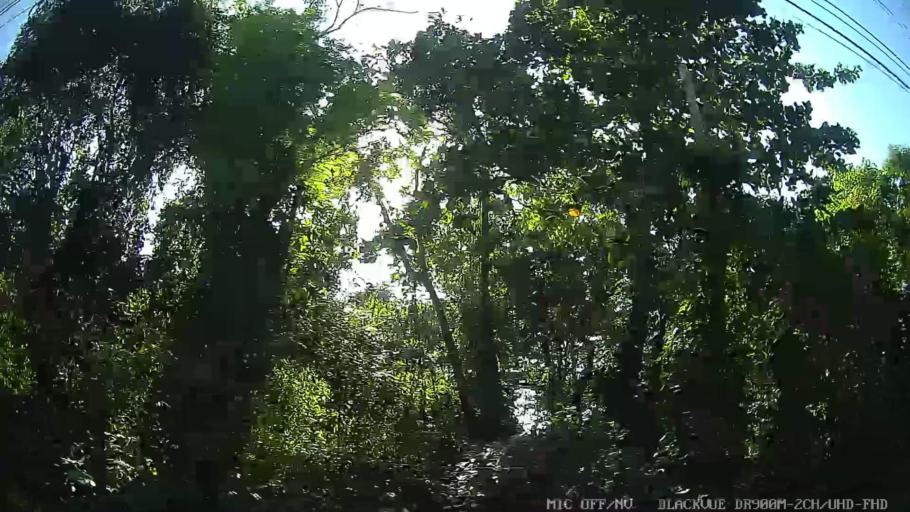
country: BR
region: Sao Paulo
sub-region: Guaruja
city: Guaruja
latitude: -24.0074
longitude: -46.2835
